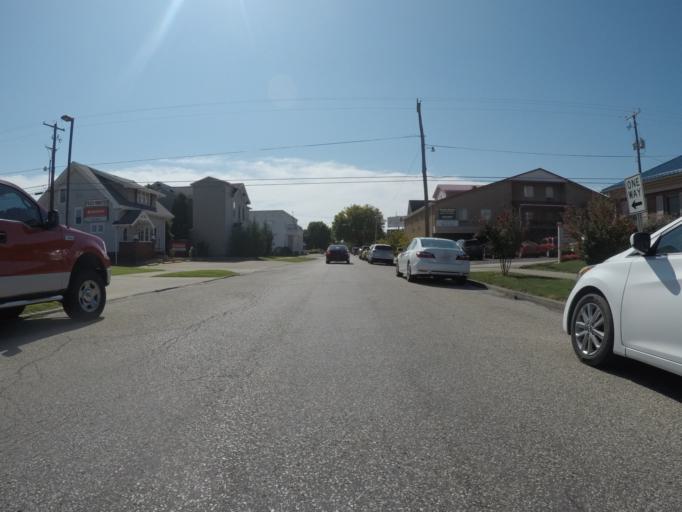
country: US
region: Ohio
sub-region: Lawrence County
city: Ironton
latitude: 38.5356
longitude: -82.6827
